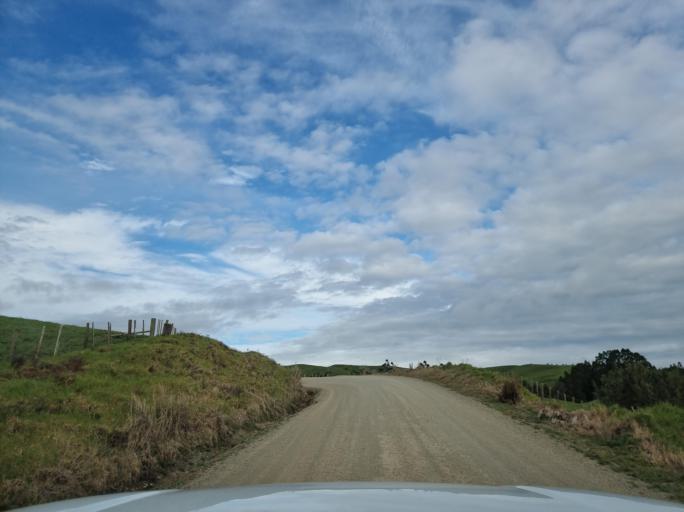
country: NZ
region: Northland
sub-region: Whangarei
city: Ruakaka
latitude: -36.0790
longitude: 174.3713
